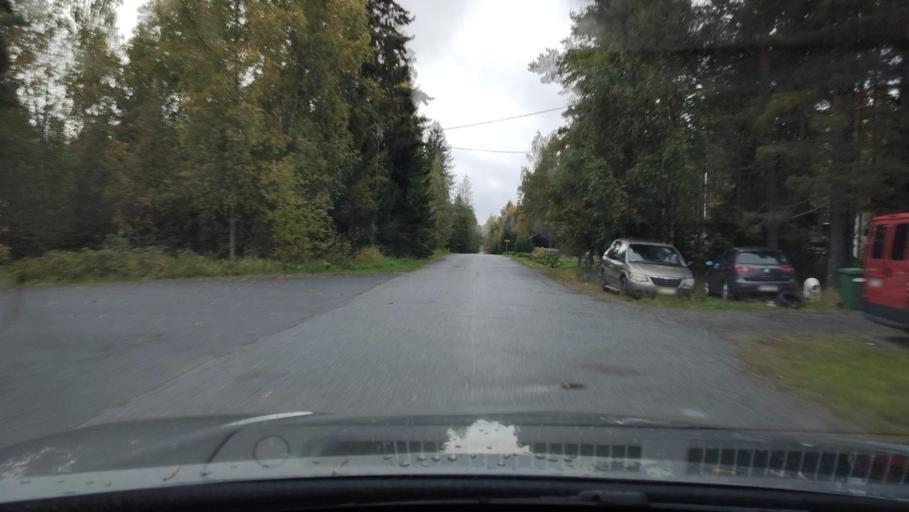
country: FI
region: Ostrobothnia
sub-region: Sydosterbotten
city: Kristinestad
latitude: 62.2650
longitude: 21.4631
